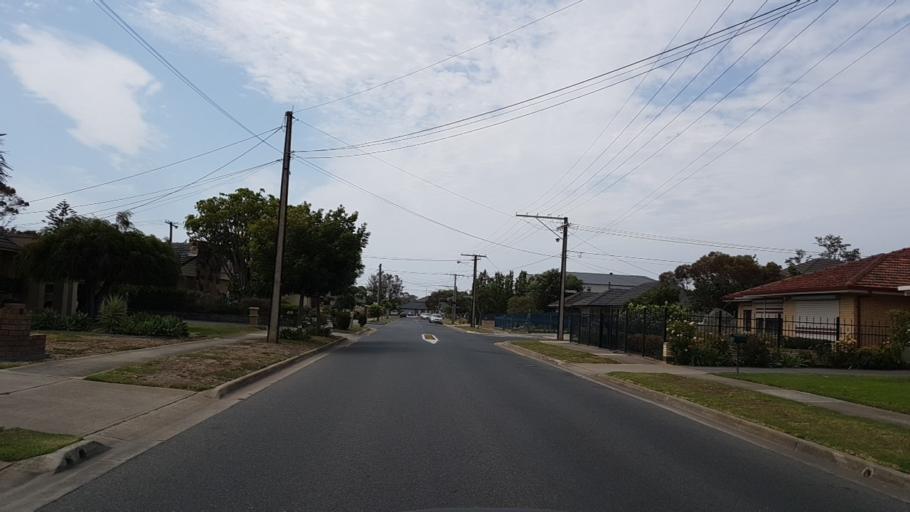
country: AU
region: South Australia
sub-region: Charles Sturt
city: Seaton
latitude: -34.9115
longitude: 138.5093
